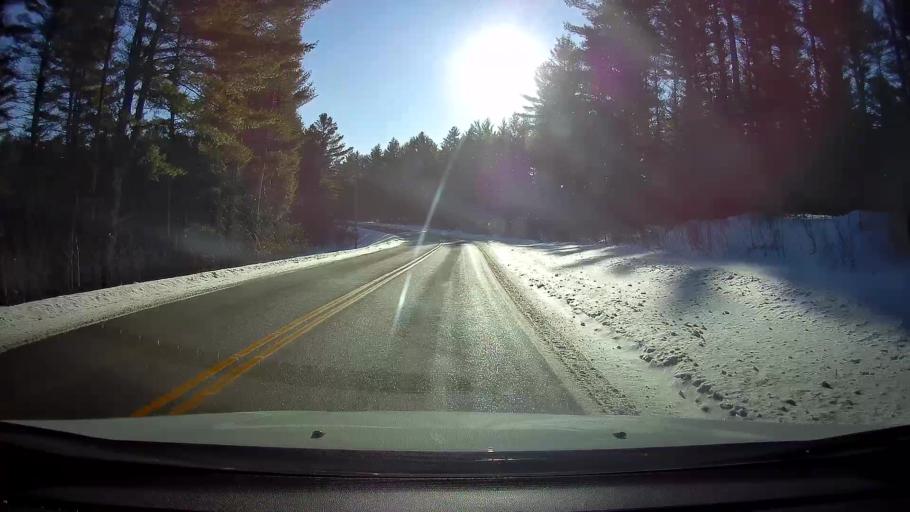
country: US
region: Wisconsin
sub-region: Sawyer County
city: Little Round Lake
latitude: 46.1130
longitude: -91.3162
